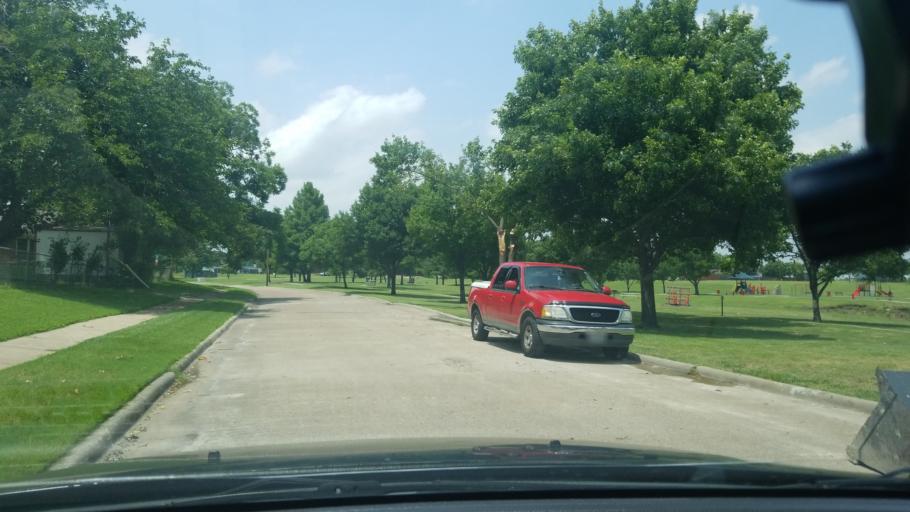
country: US
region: Texas
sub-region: Dallas County
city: Mesquite
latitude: 32.8022
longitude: -96.6350
